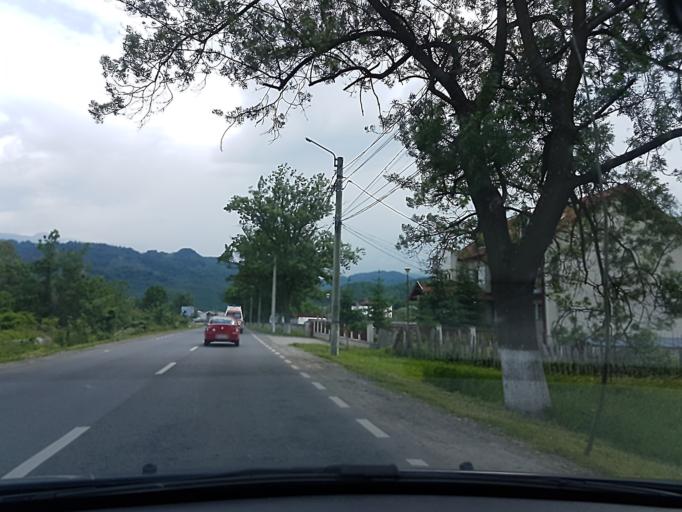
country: RO
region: Hunedoara
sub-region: Comuna Aninoasa
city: Iscroni
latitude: 45.3744
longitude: 23.3481
